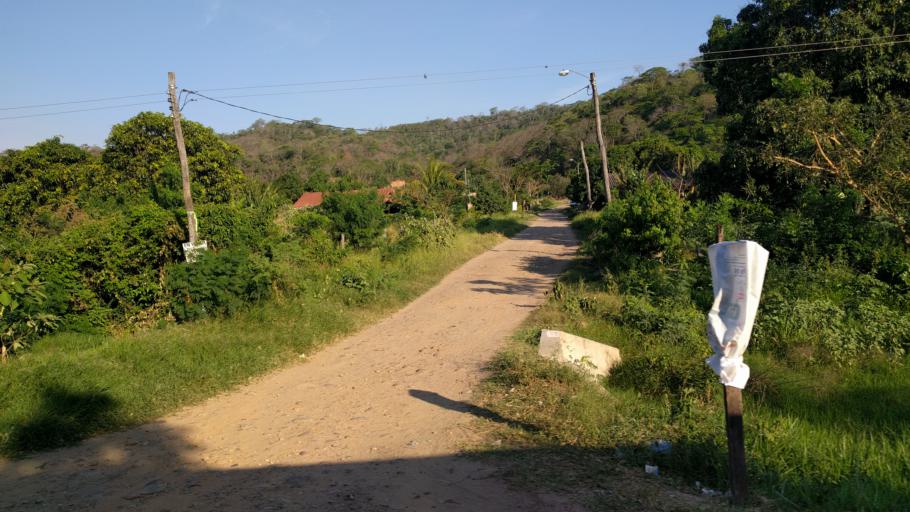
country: BO
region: Santa Cruz
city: Jorochito
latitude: -18.0669
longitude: -63.4374
